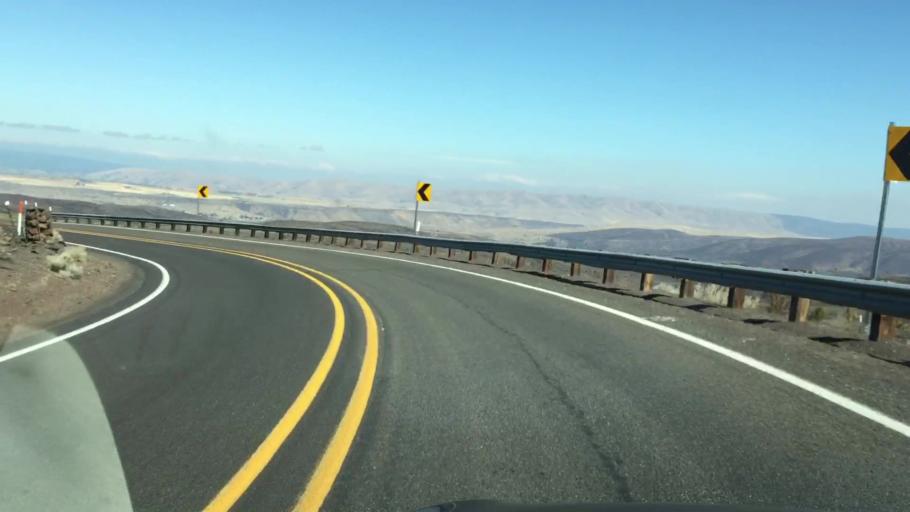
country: US
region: Oregon
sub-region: Jefferson County
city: Warm Springs
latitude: 45.1151
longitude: -121.0403
